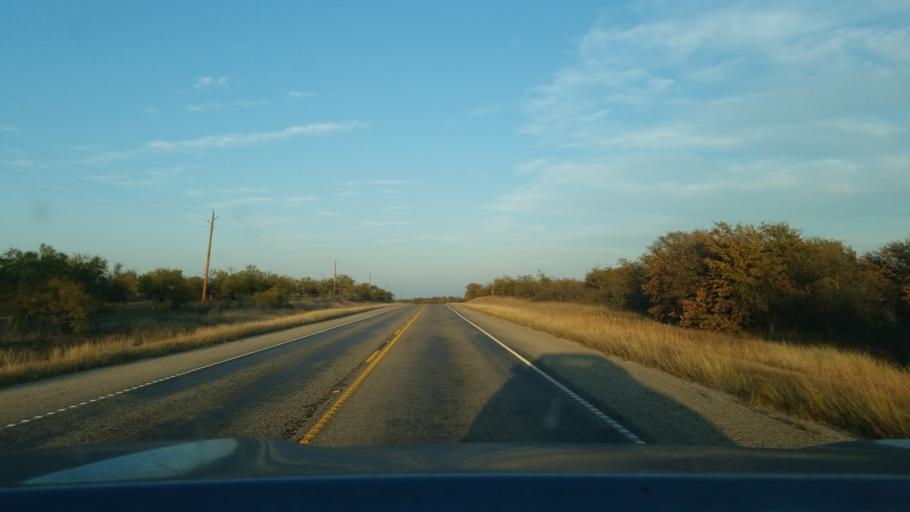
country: US
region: Texas
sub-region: Eastland County
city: Cisco
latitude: 32.4067
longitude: -98.9529
